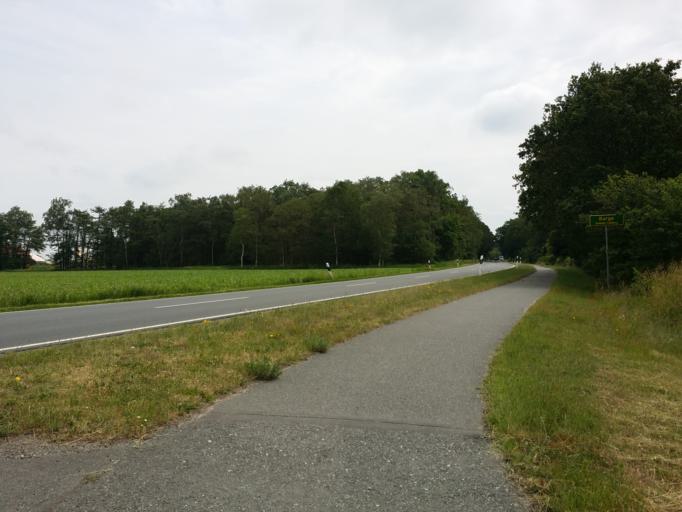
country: DE
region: Lower Saxony
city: Friedeburg
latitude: 53.4187
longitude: 7.8777
